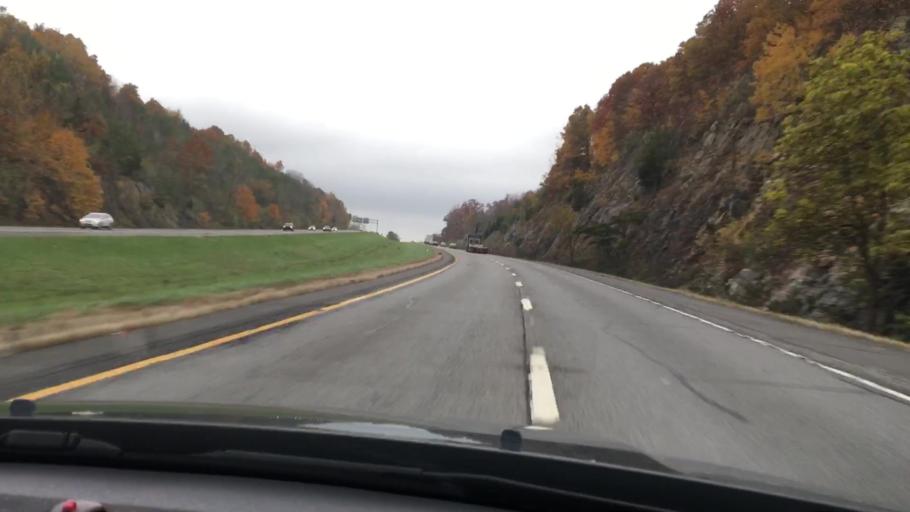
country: US
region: New York
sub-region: Putnam County
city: Brewster
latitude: 41.4019
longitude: -73.6028
